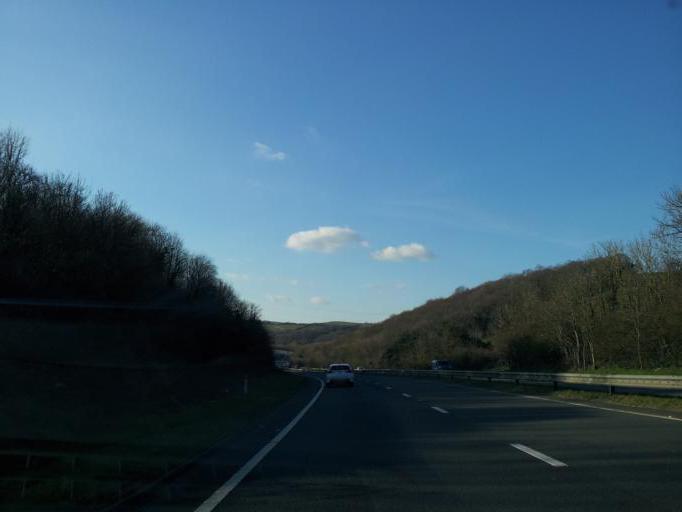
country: GB
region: England
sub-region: Devon
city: Exeter
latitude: 50.7135
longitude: -3.5698
